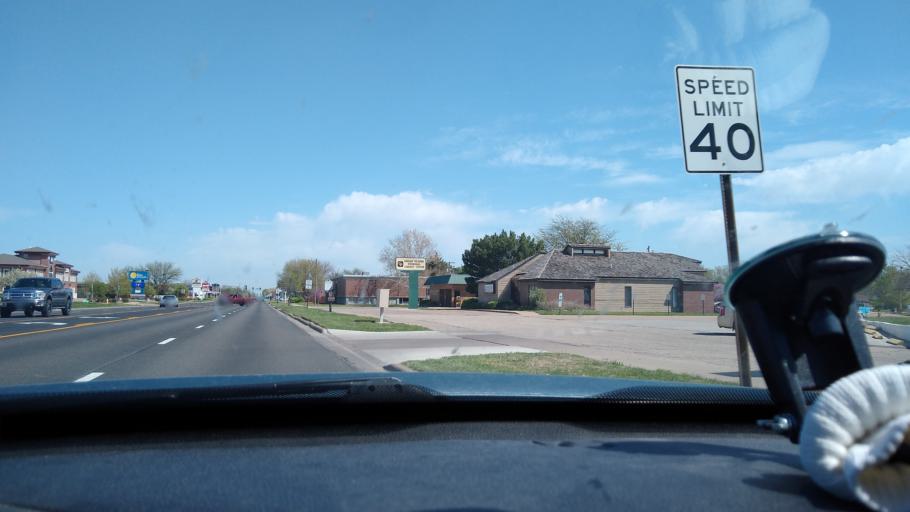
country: US
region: Kansas
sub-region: Saline County
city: Salina
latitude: 38.8055
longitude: -97.5942
